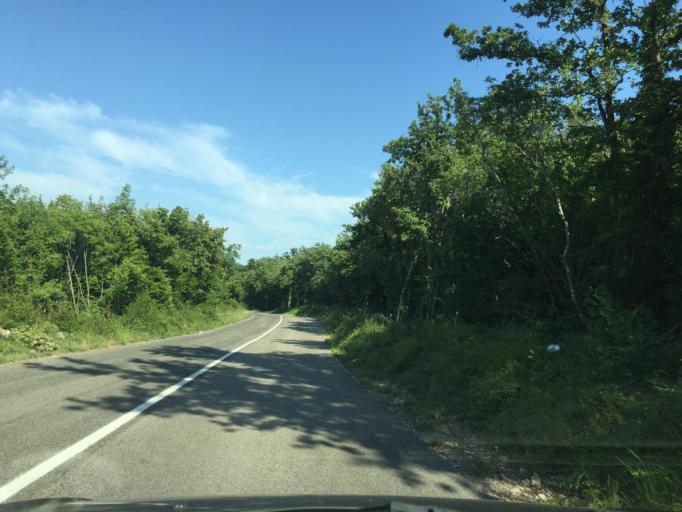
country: HR
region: Primorsko-Goranska
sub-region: Grad Crikvenica
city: Crikvenica
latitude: 45.1291
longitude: 14.6284
